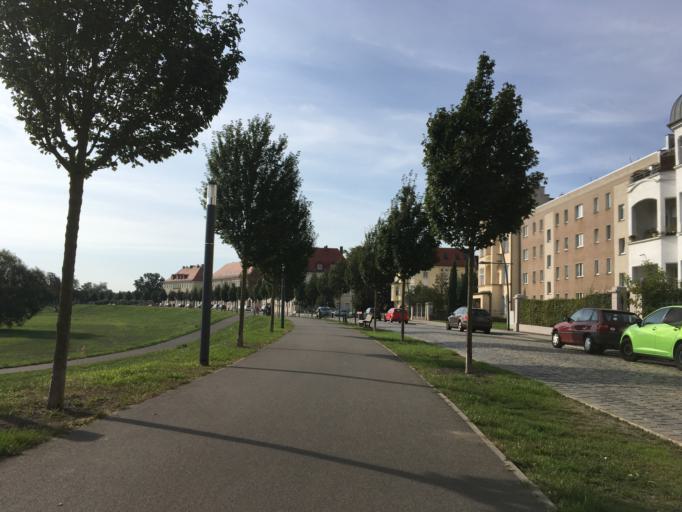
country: DE
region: Brandenburg
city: Forst
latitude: 51.7418
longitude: 14.6549
